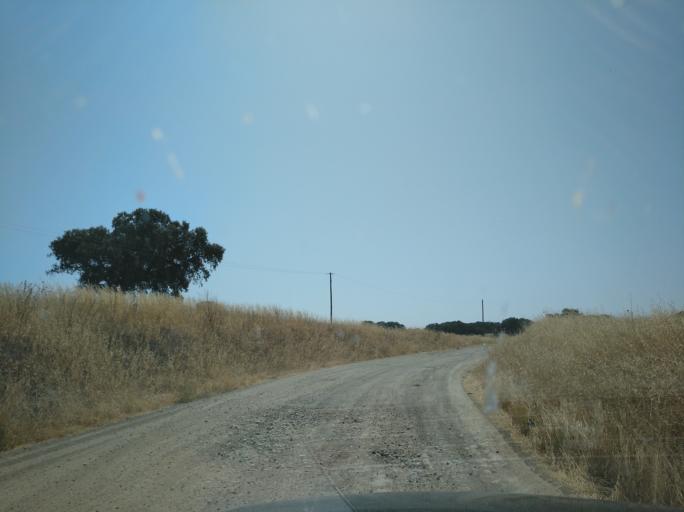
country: PT
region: Portalegre
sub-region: Campo Maior
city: Campo Maior
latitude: 39.0290
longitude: -6.9782
